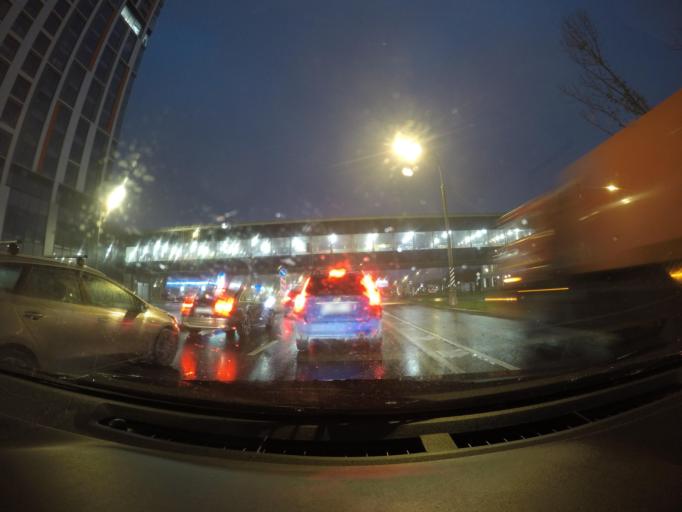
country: RU
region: Moskovskaya
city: Kozhukhovo
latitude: 55.6943
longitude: 37.6663
